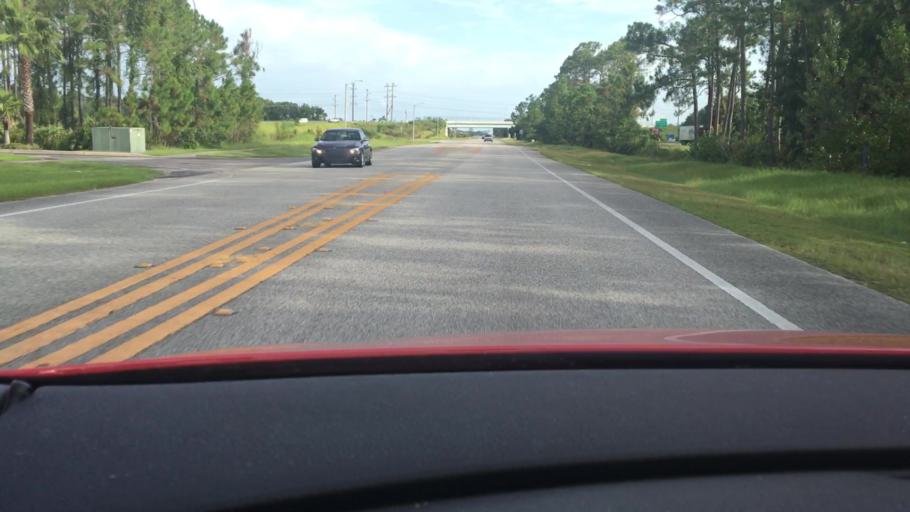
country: US
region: Florida
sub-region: Volusia County
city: Daytona Beach
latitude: 29.1941
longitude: -81.0948
